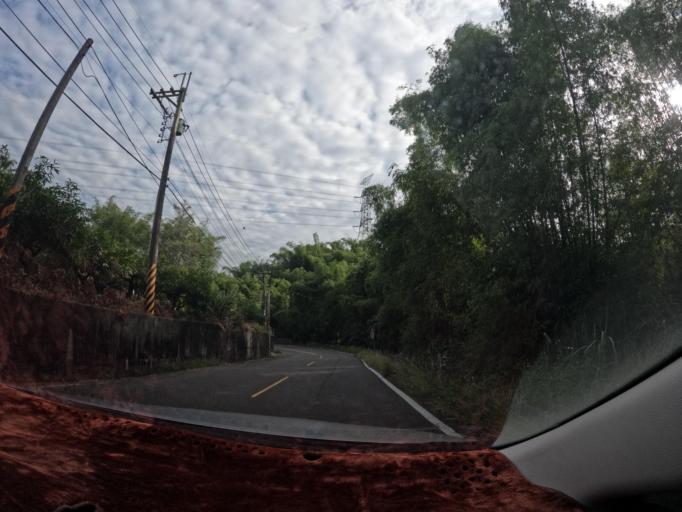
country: TW
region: Taiwan
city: Yujing
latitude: 23.0211
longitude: 120.4120
